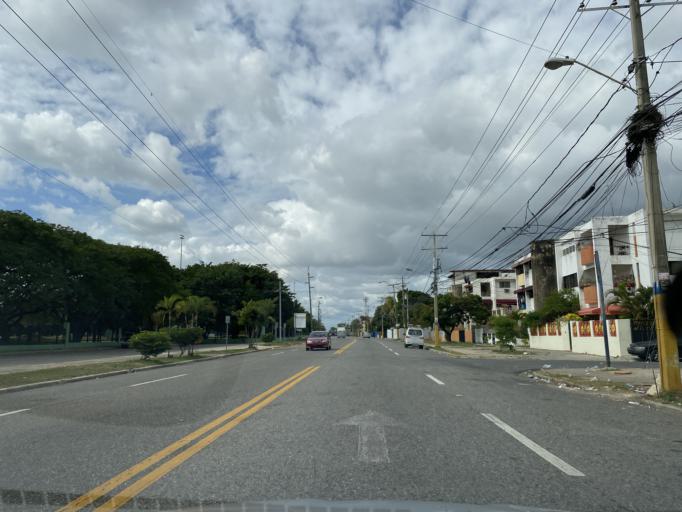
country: DO
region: Santo Domingo
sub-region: Santo Domingo
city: Santo Domingo Este
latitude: 18.4816
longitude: -69.8495
